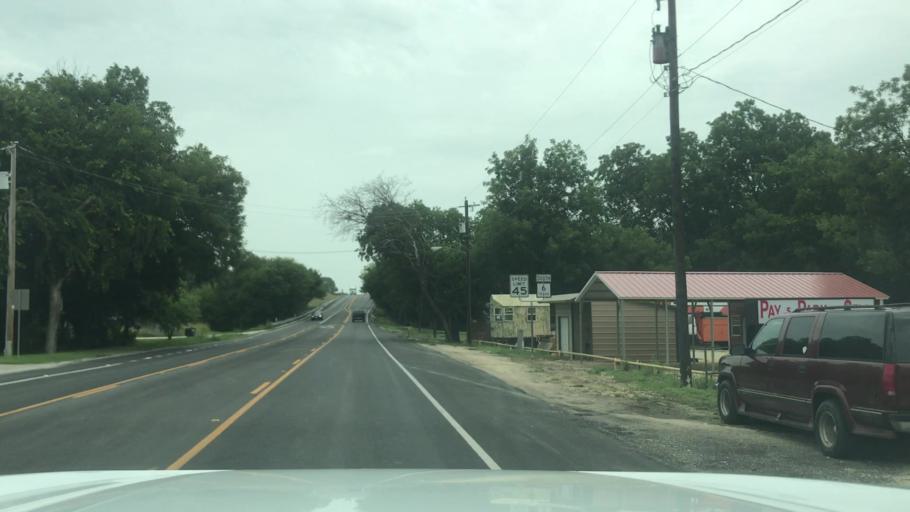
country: US
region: Texas
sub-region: Hamilton County
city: Hico
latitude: 31.9819
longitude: -98.0283
